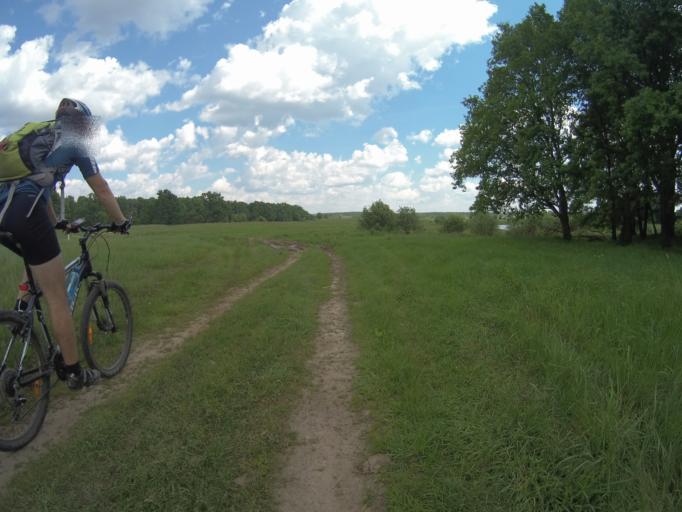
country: RU
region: Vladimir
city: Vorsha
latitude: 56.0283
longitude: 40.2036
